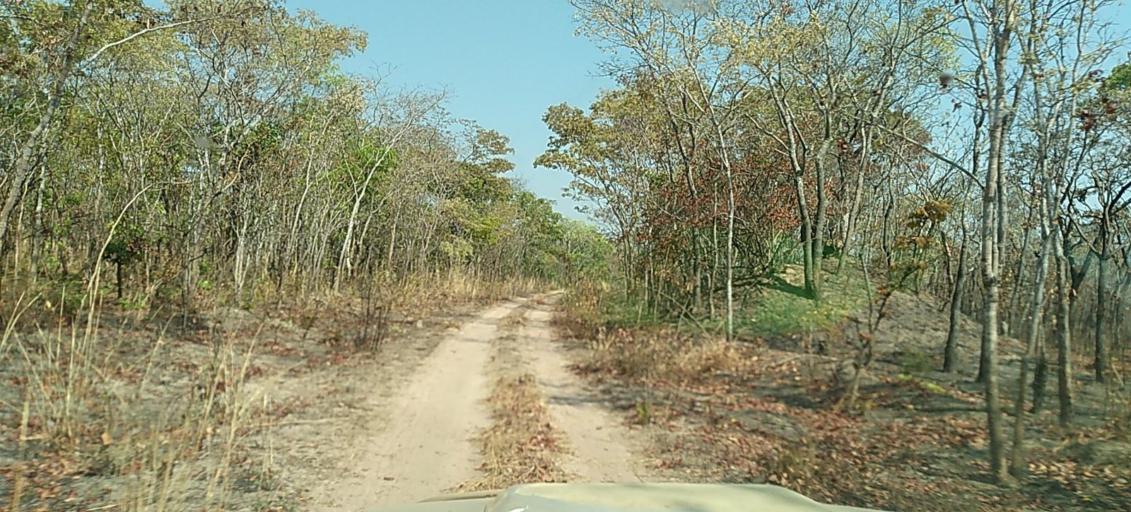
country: ZM
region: North-Western
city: Kalengwa
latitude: -13.3269
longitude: 24.8301
